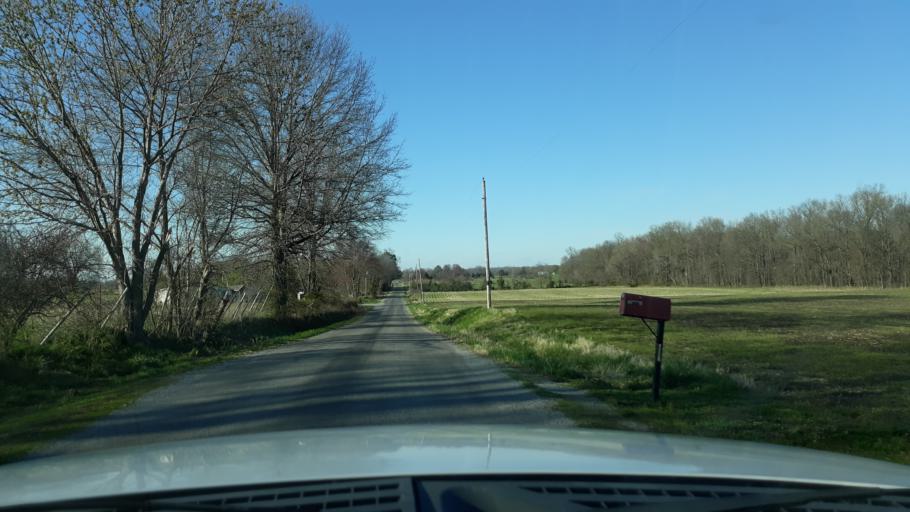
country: US
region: Illinois
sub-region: Saline County
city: Harrisburg
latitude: 37.7888
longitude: -88.6056
